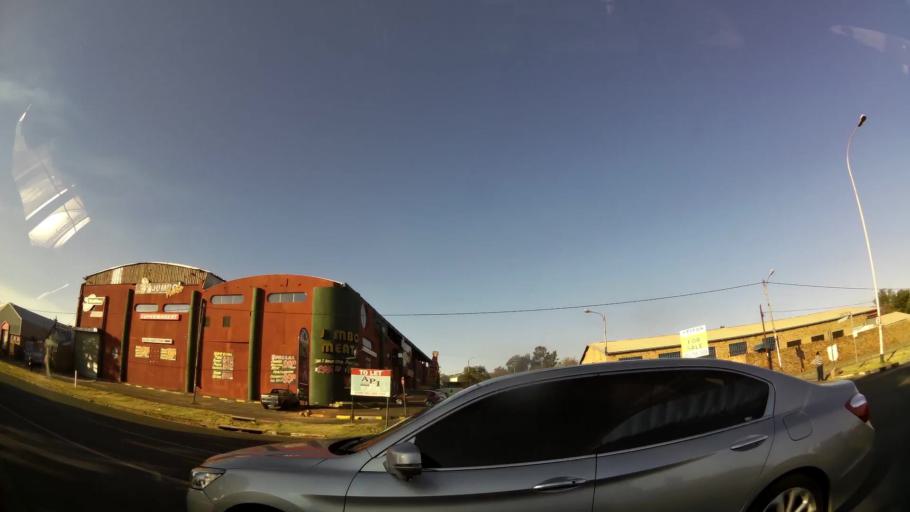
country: ZA
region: Gauteng
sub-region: City of Johannesburg Metropolitan Municipality
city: Roodepoort
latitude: -26.1474
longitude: 27.8628
